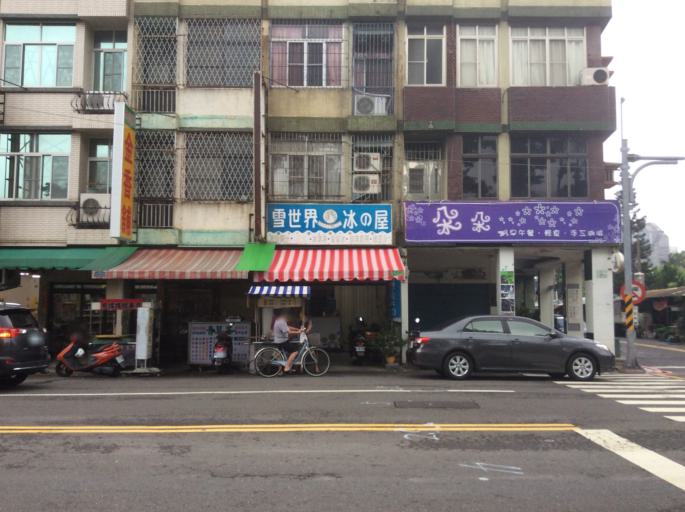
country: TW
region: Kaohsiung
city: Kaohsiung
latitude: 22.6080
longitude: 120.3082
